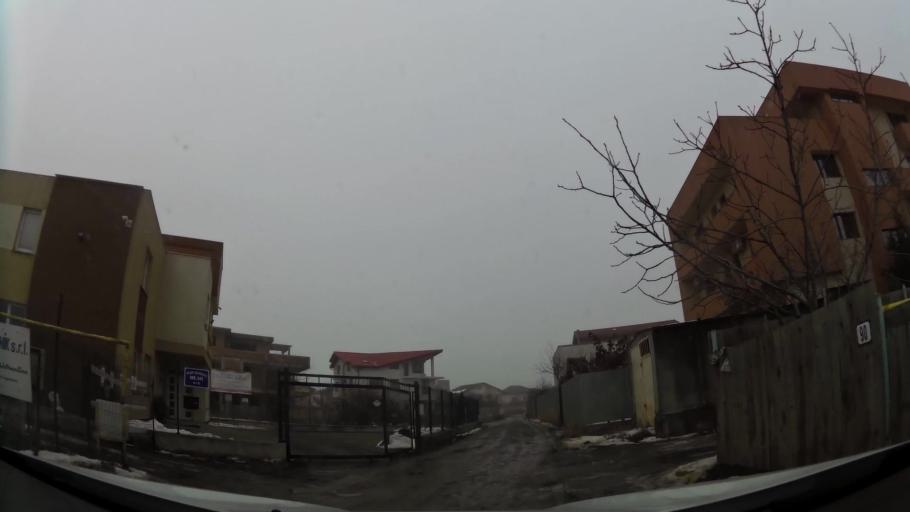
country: RO
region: Ilfov
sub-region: Comuna Chiajna
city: Rosu
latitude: 44.4388
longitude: 25.9964
